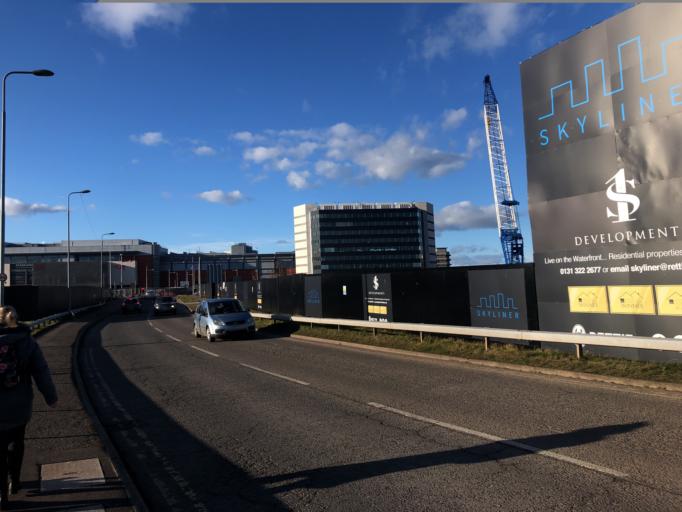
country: GB
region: Scotland
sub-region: West Lothian
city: Seafield
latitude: 55.9795
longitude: -3.1724
